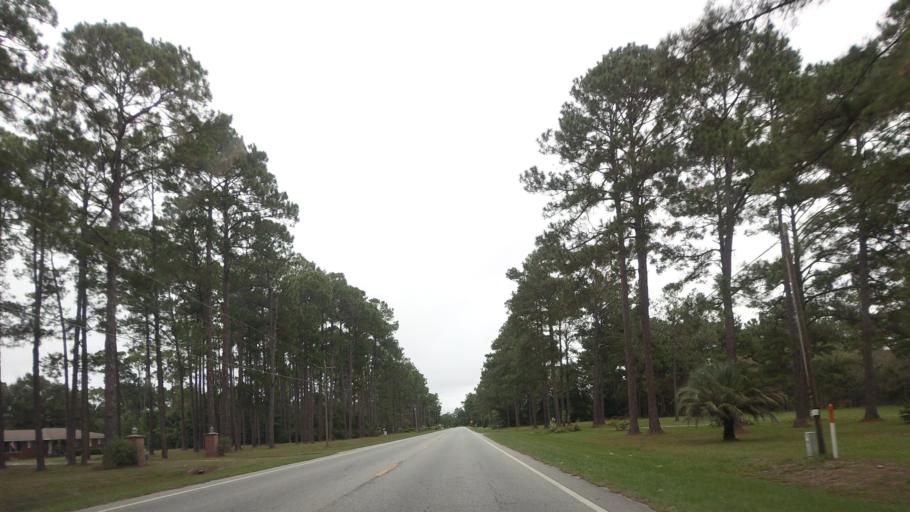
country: US
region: Georgia
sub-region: Berrien County
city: Ray City
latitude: 31.0586
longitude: -83.1975
